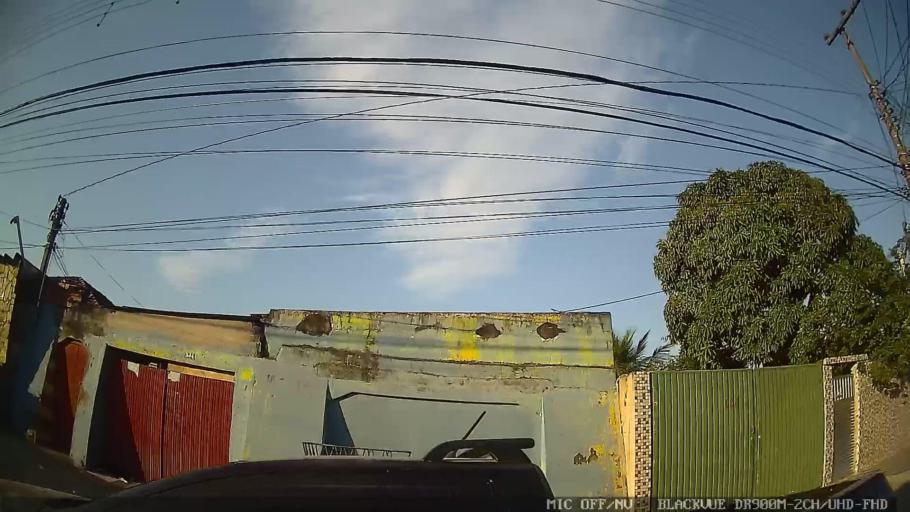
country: BR
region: Sao Paulo
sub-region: Guaruja
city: Guaruja
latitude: -23.9870
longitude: -46.2763
